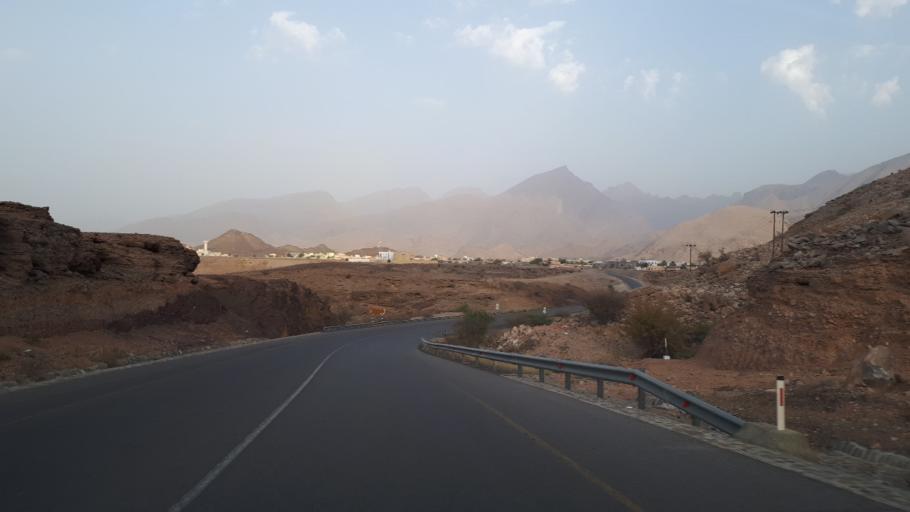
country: OM
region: Al Batinah
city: Rustaq
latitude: 23.3915
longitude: 57.1838
